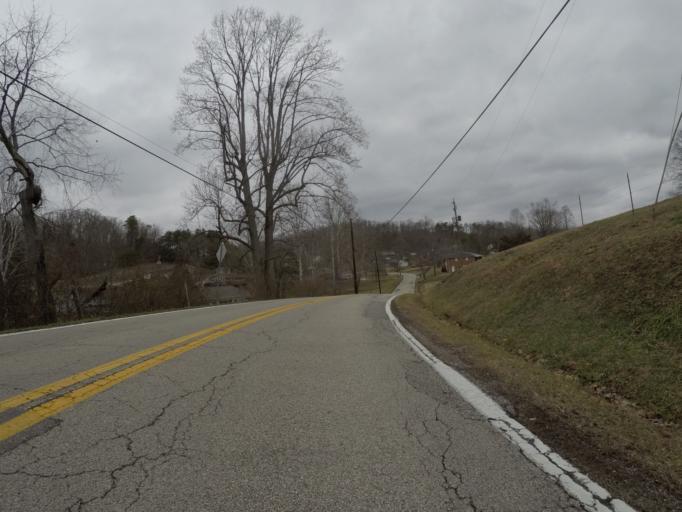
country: US
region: West Virginia
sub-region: Cabell County
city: Barboursville
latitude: 38.4348
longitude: -82.2444
